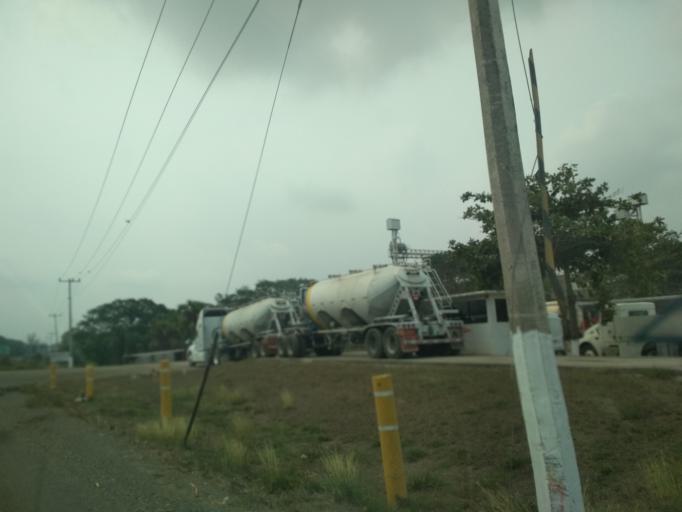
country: MX
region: Veracruz
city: Paso del Toro
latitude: 19.0309
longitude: -96.1456
